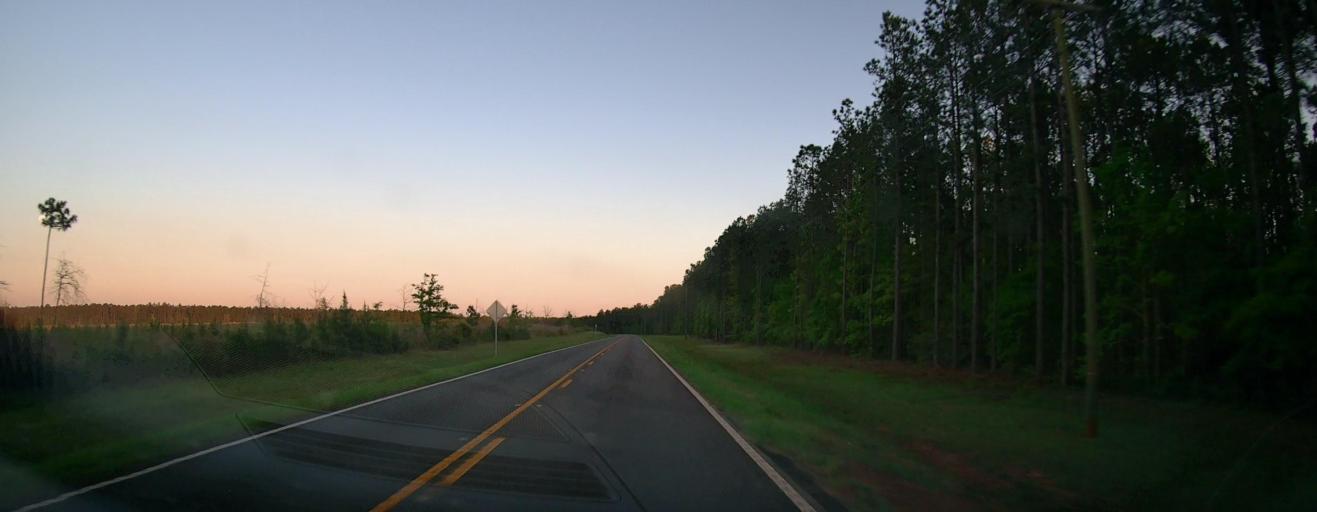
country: US
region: Georgia
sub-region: Marion County
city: Buena Vista
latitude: 32.3848
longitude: -84.5646
